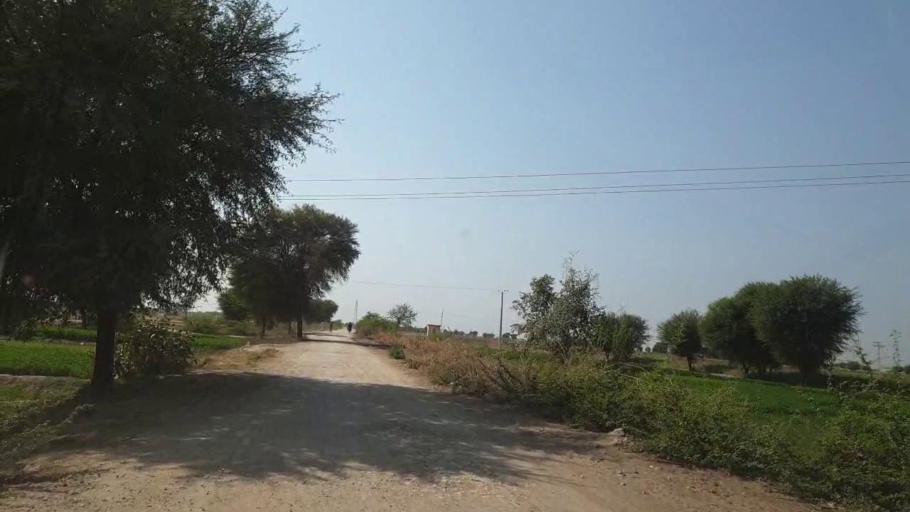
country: PK
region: Sindh
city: Nabisar
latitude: 25.0381
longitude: 69.5164
